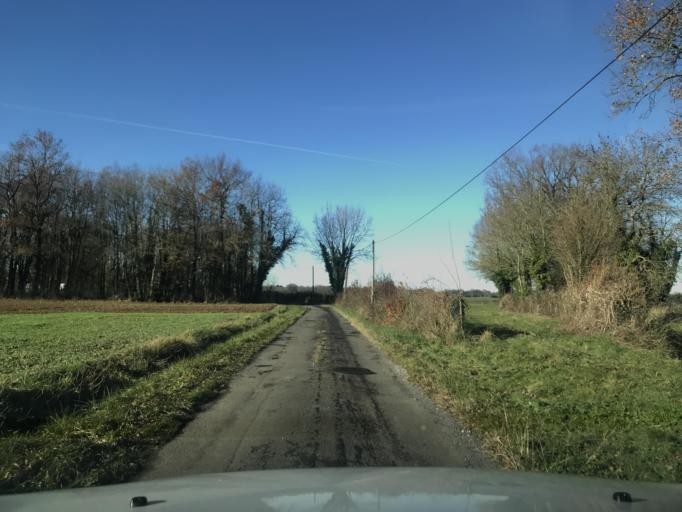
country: FR
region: Poitou-Charentes
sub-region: Departement de la Charente
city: Saint-Claud
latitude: 45.8502
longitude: 0.4989
